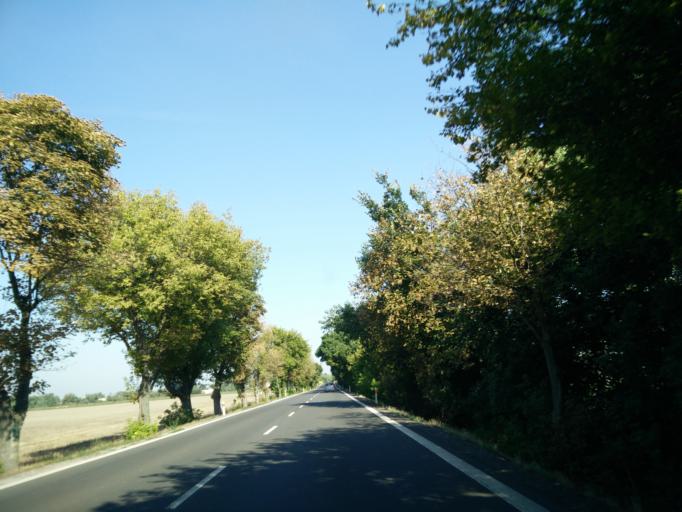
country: SK
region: Nitriansky
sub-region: Okres Nitra
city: Nitra
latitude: 48.3652
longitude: 18.0455
